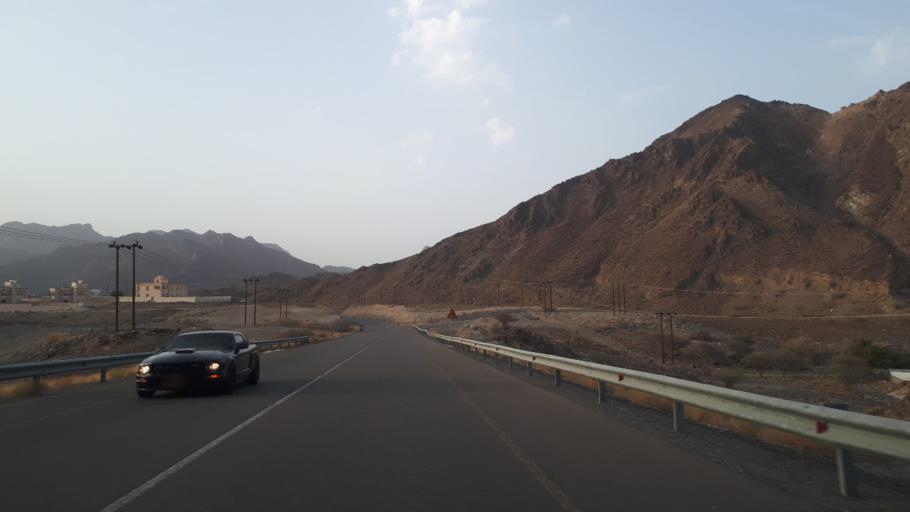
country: OM
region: Al Batinah
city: Rustaq
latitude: 23.4141
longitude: 57.2611
